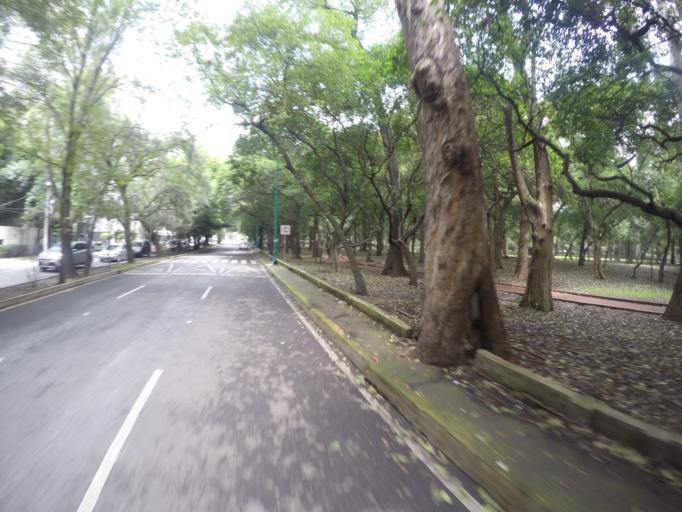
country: MX
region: Mexico City
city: Miguel Hidalgo
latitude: 19.4292
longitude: -99.1839
